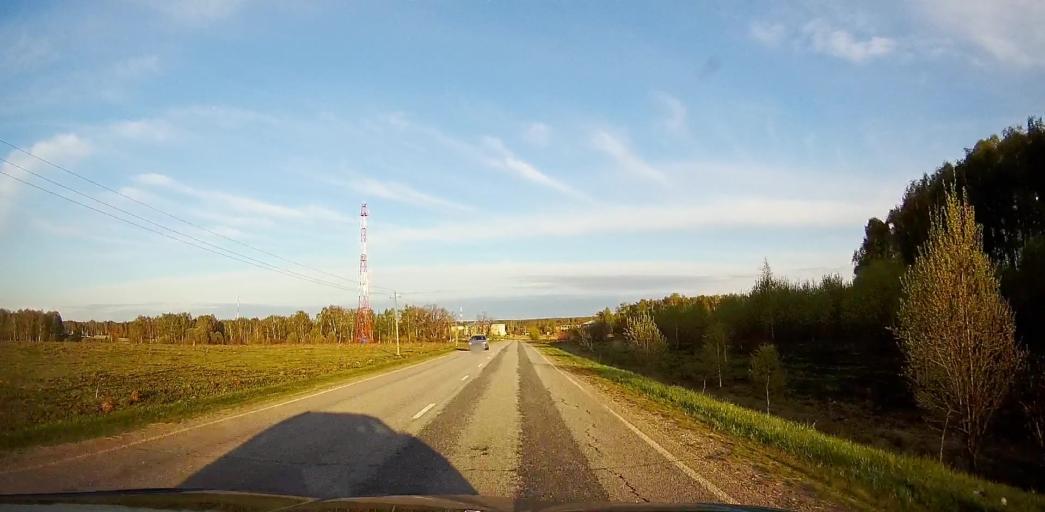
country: RU
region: Moskovskaya
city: Meshcherino
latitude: 55.2353
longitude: 38.3541
